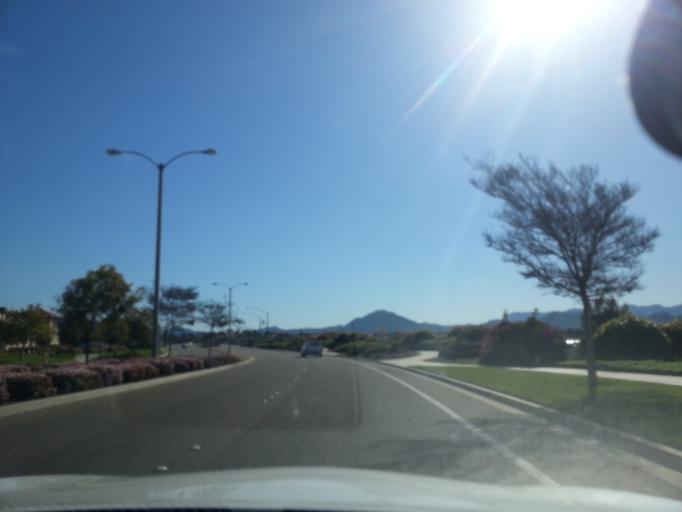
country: US
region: California
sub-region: Ventura County
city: Camarillo
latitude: 34.2160
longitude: -119.0739
